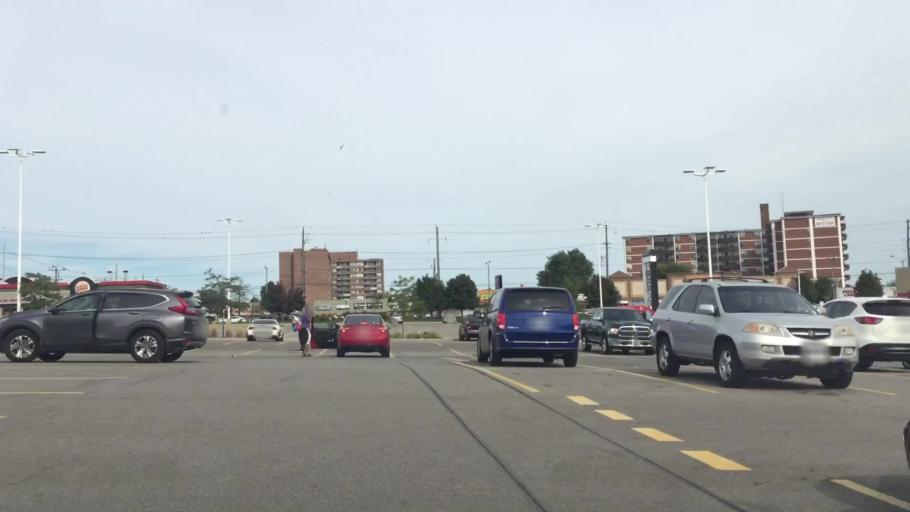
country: CA
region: Ontario
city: Scarborough
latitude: 43.7588
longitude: -79.2271
